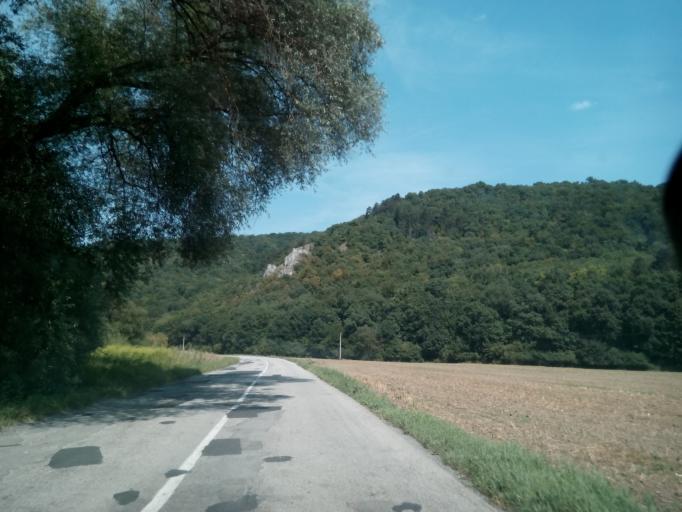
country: SK
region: Kosicky
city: Kosice
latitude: 48.8185
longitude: 21.2349
